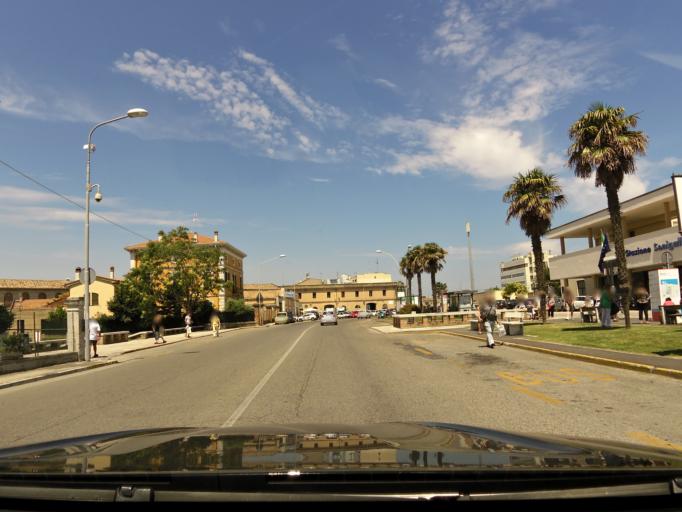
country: IT
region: The Marches
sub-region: Provincia di Ancona
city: Senigallia
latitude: 43.7156
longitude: 13.2215
